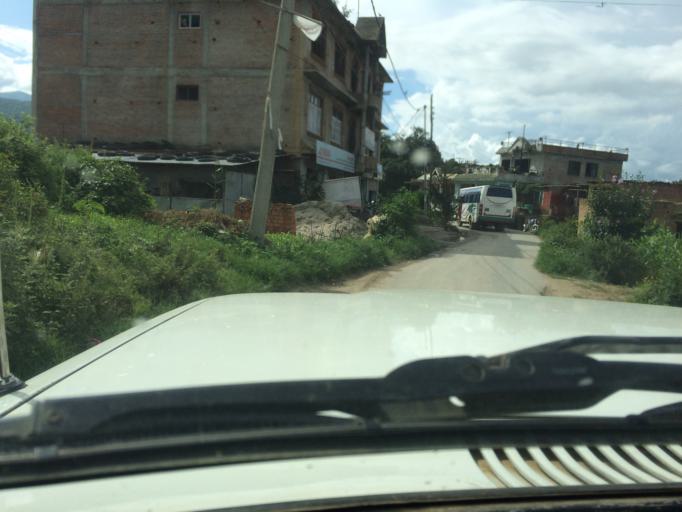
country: NP
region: Central Region
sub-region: Bagmati Zone
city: Patan
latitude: 27.6150
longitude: 85.3072
